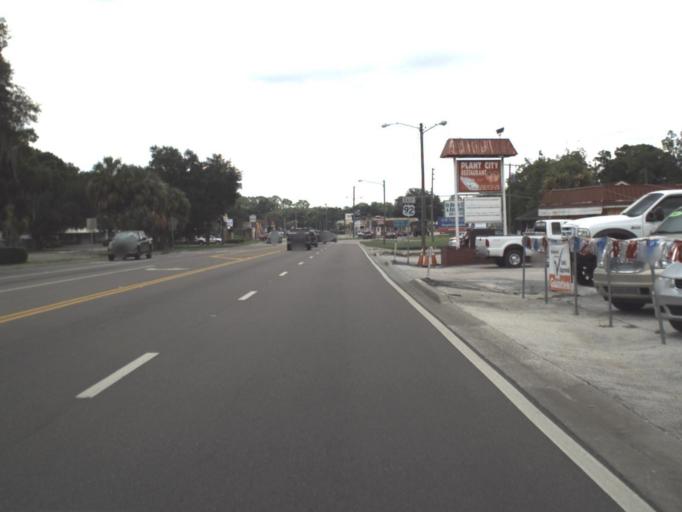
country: US
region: Florida
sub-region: Hillsborough County
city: Plant City
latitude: 28.0188
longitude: -82.1438
